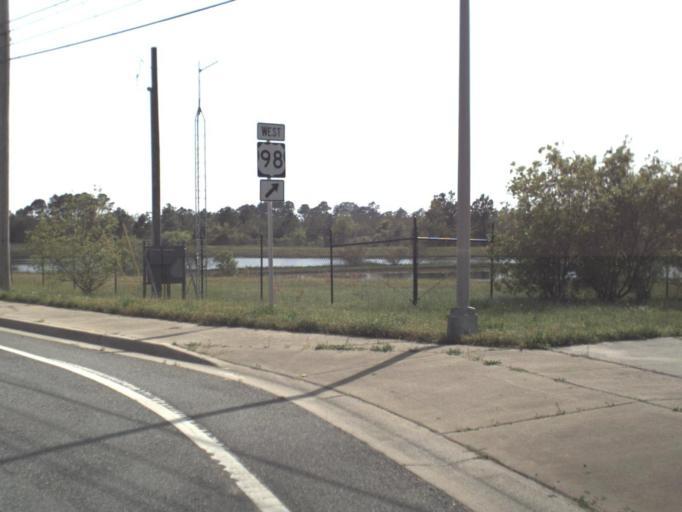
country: US
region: Florida
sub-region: Santa Rosa County
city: Navarre
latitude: 30.4055
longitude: -86.8712
